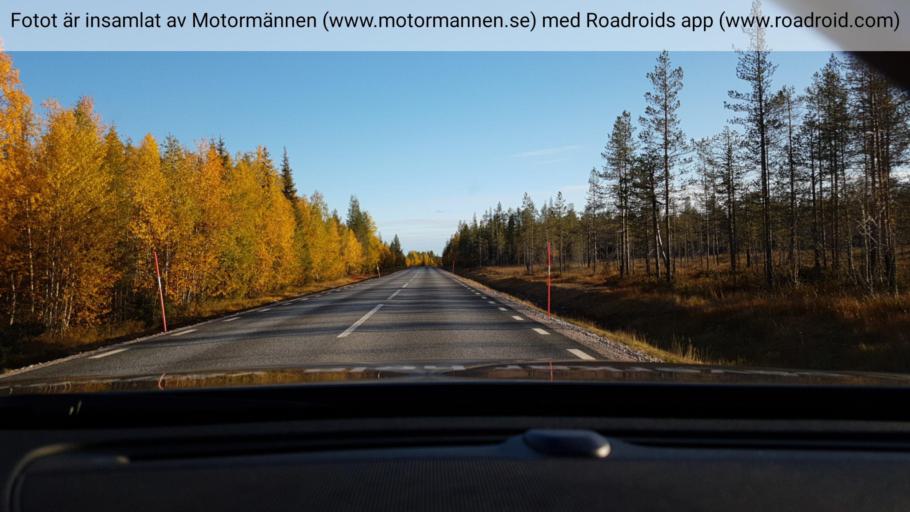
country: SE
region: Norrbotten
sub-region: Jokkmokks Kommun
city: Jokkmokk
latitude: 66.7948
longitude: 19.8814
